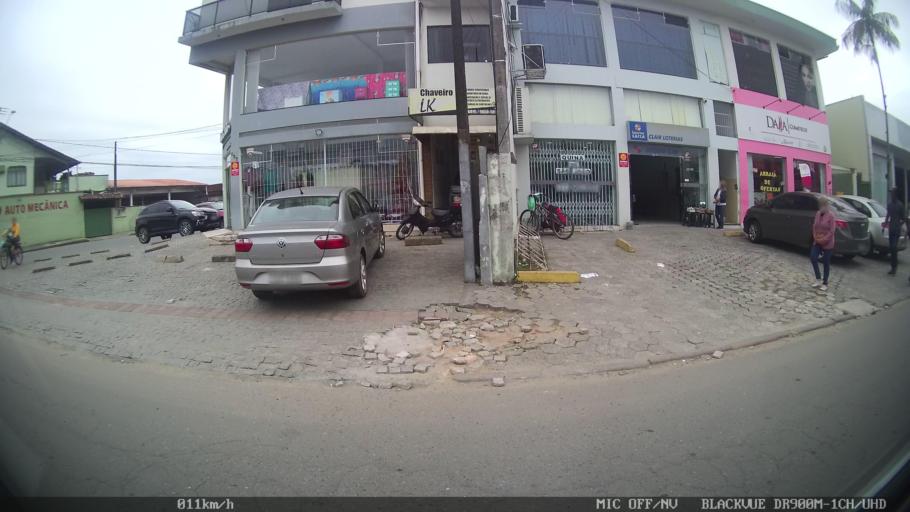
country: BR
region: Santa Catarina
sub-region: Joinville
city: Joinville
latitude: -26.3340
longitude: -48.8170
